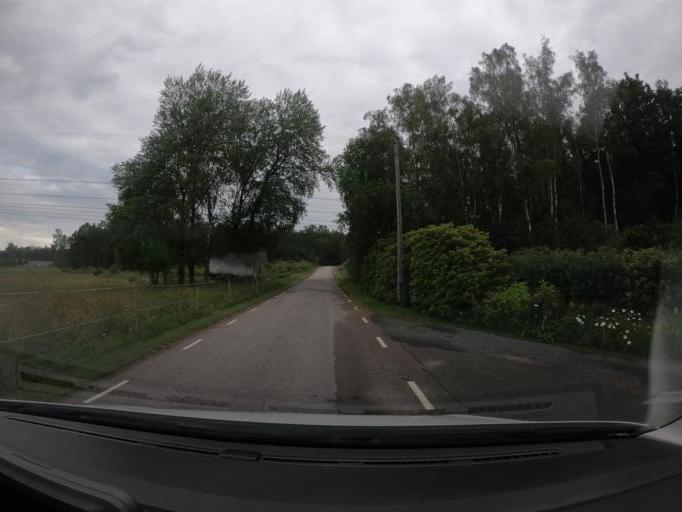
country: SE
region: Skane
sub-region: Klippans Kommun
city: Klippan
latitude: 56.2797
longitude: 13.1252
